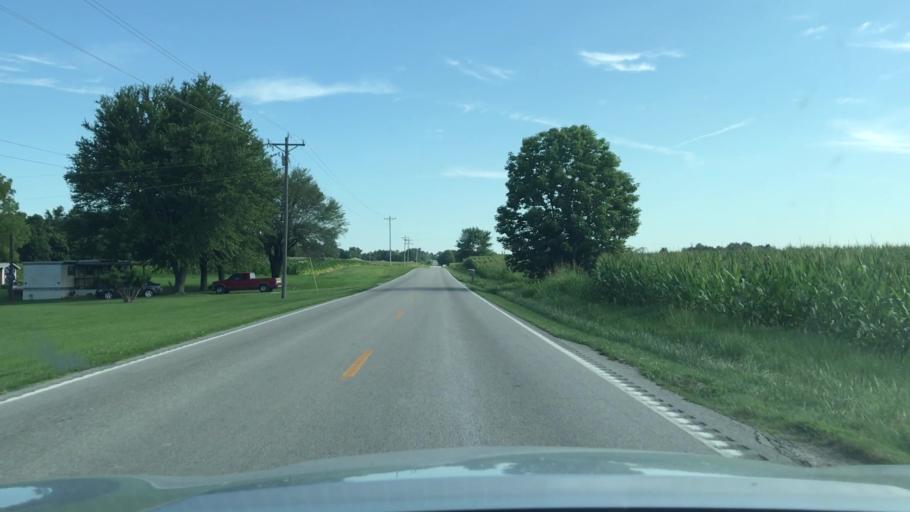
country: US
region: Kentucky
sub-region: Todd County
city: Elkton
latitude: 36.9171
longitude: -87.1630
